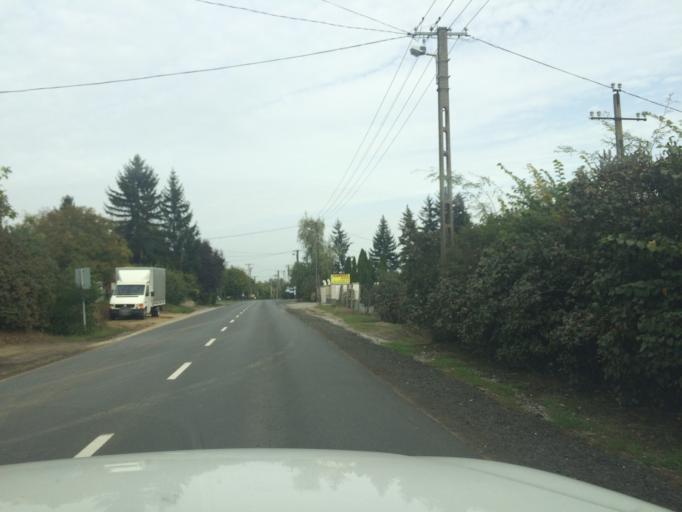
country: HU
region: Szabolcs-Szatmar-Bereg
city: Kotaj
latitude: 48.0072
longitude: 21.7372
